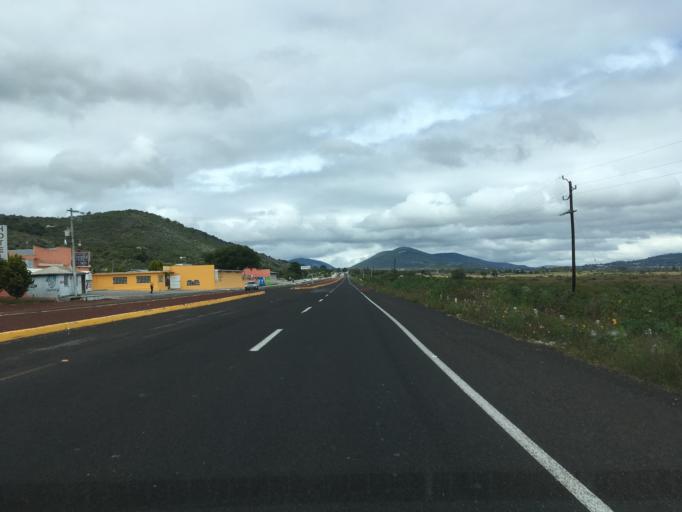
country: MX
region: Hidalgo
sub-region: Atotonilco el Grande
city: Santa Maria Amajac
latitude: 20.3489
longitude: -98.7131
